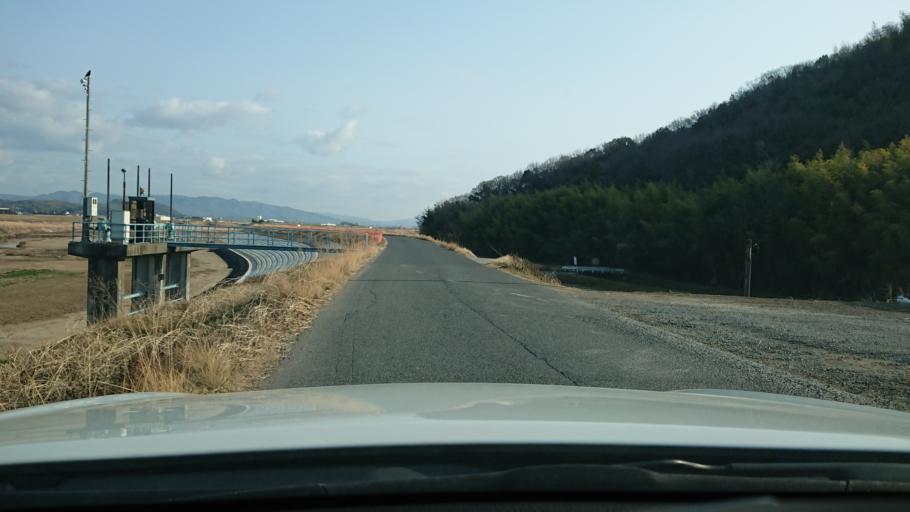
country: JP
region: Okayama
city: Soja
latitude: 34.6246
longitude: 133.7050
